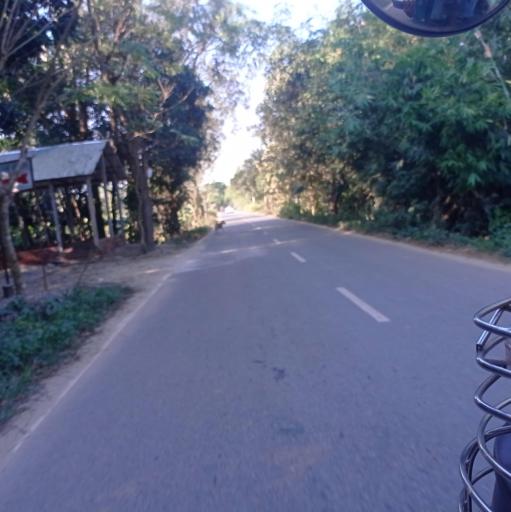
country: BD
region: Dhaka
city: Bajitpur
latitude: 24.1537
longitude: 90.8116
